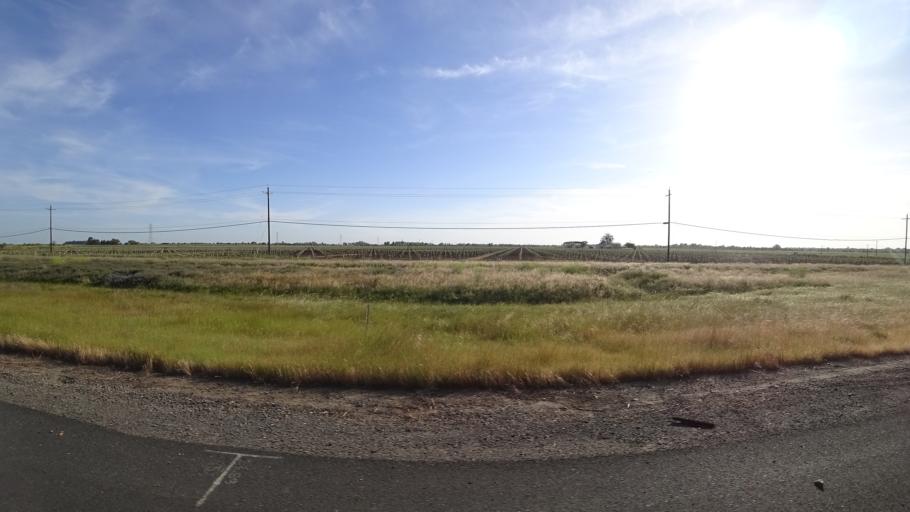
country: US
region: California
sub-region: Placer County
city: Sheridan
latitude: 38.9888
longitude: -121.3878
